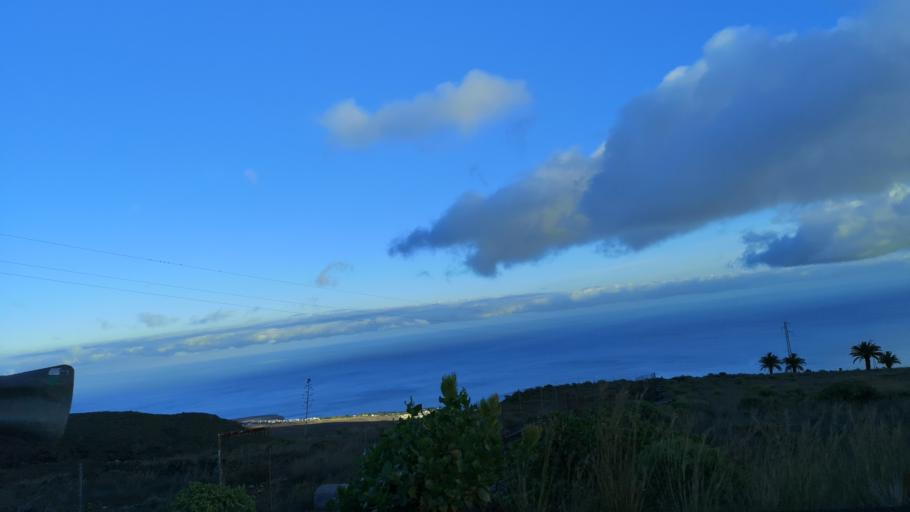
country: ES
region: Canary Islands
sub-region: Provincia de Santa Cruz de Tenerife
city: Alajero
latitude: 28.0503
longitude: -17.2317
